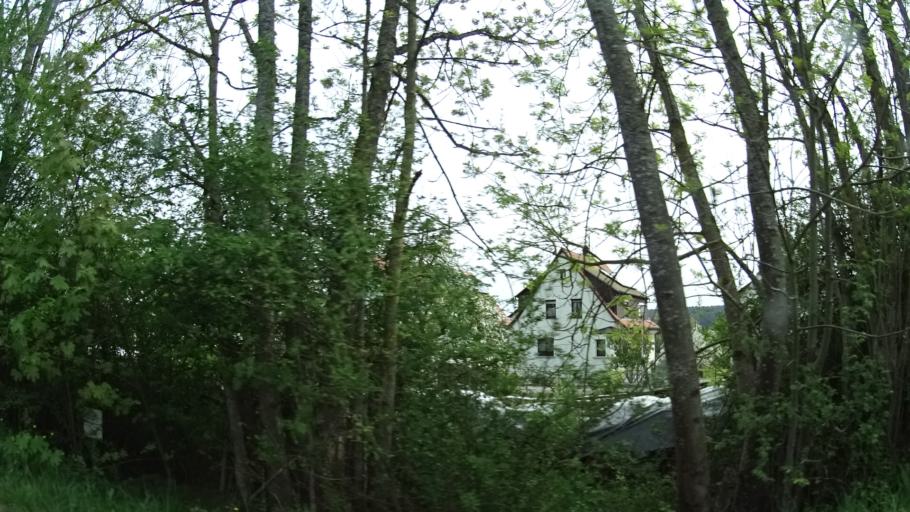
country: DE
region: Baden-Wuerttemberg
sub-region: Freiburg Region
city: Deisslingen
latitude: 48.1293
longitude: 8.6269
